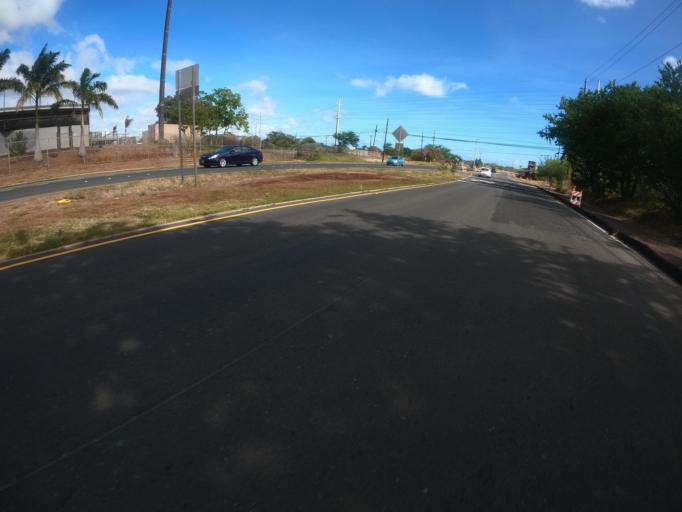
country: US
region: Hawaii
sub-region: Honolulu County
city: Makakilo City
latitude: 21.3255
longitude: -158.0686
